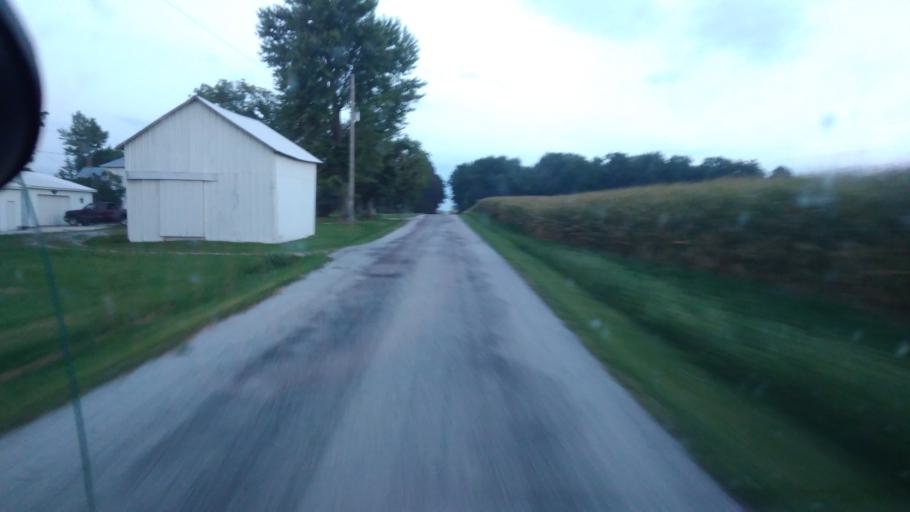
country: US
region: Ohio
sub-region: Hardin County
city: Kenton
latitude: 40.6560
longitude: -83.4588
